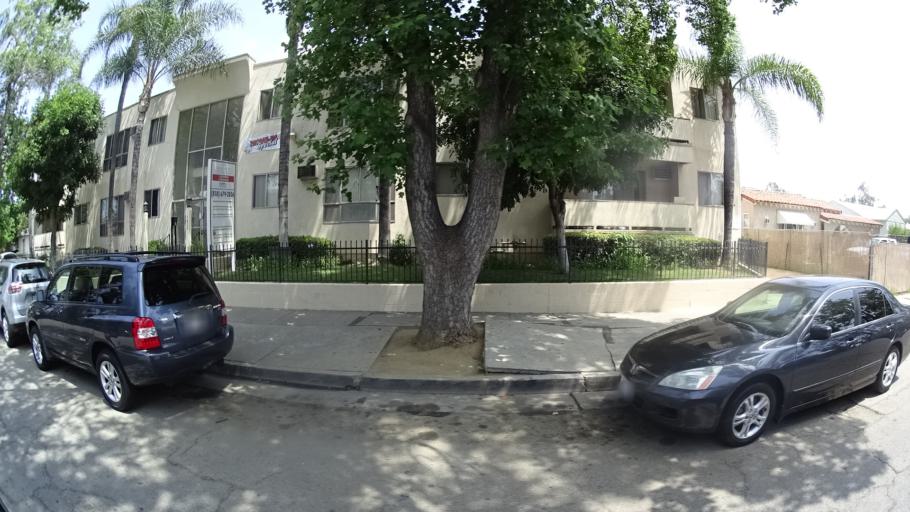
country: US
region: California
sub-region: Los Angeles County
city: Van Nuys
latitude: 34.1876
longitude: -118.4561
